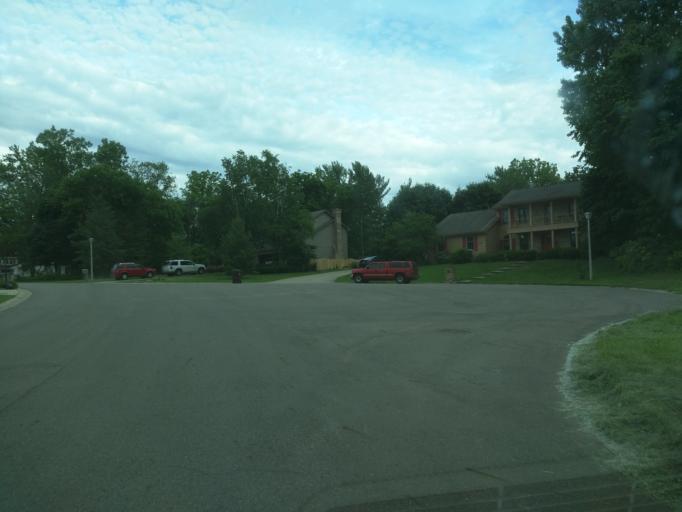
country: US
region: Michigan
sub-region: Eaton County
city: Waverly
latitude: 42.7526
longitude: -84.6149
